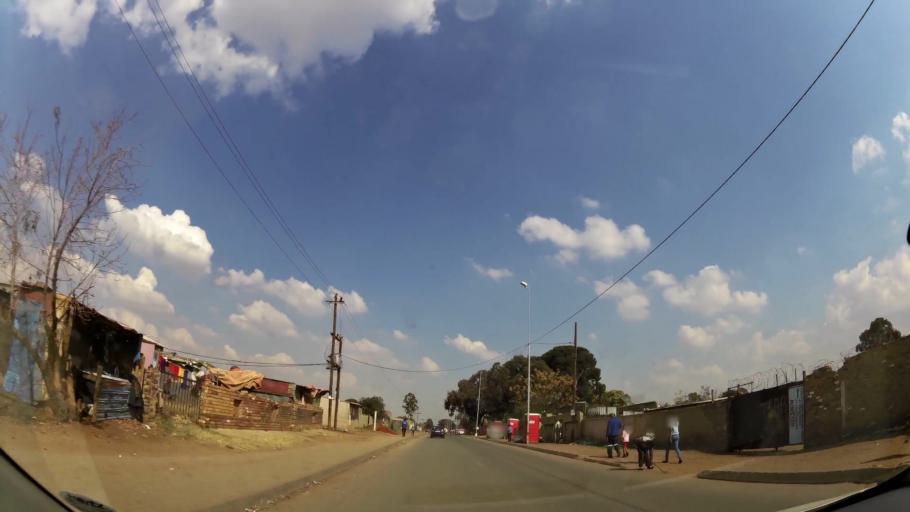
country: ZA
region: Gauteng
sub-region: Ekurhuleni Metropolitan Municipality
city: Germiston
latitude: -26.3164
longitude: 28.1449
